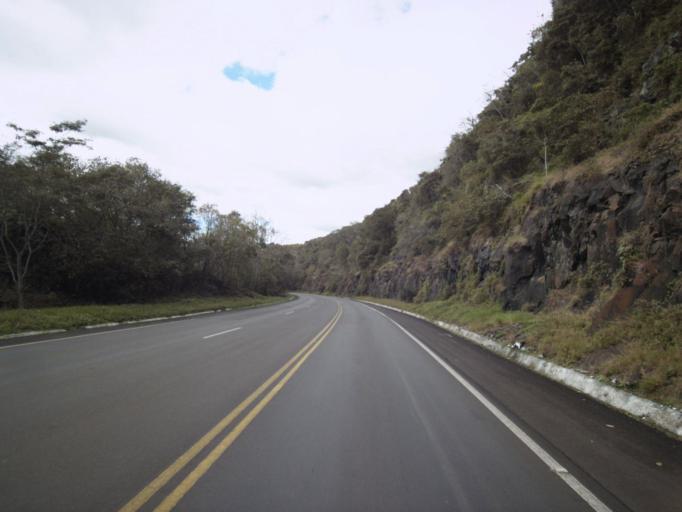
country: BR
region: Santa Catarina
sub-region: Concordia
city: Concordia
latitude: -27.3673
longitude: -51.9965
